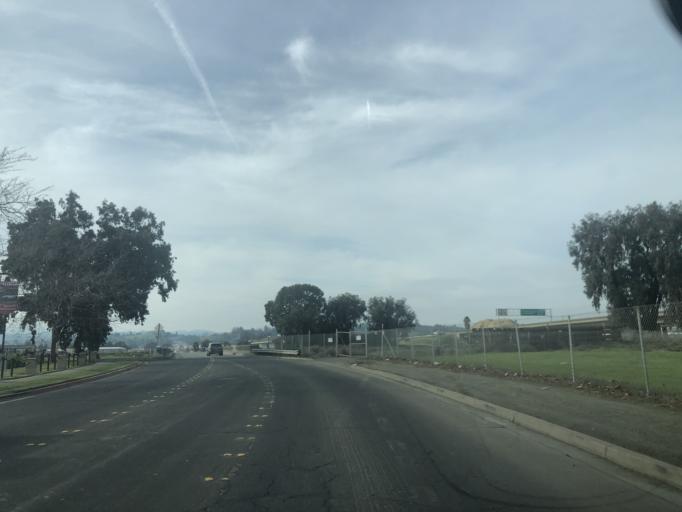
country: US
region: California
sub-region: Contra Costa County
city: Pacheco
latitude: 37.9994
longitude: -122.0551
